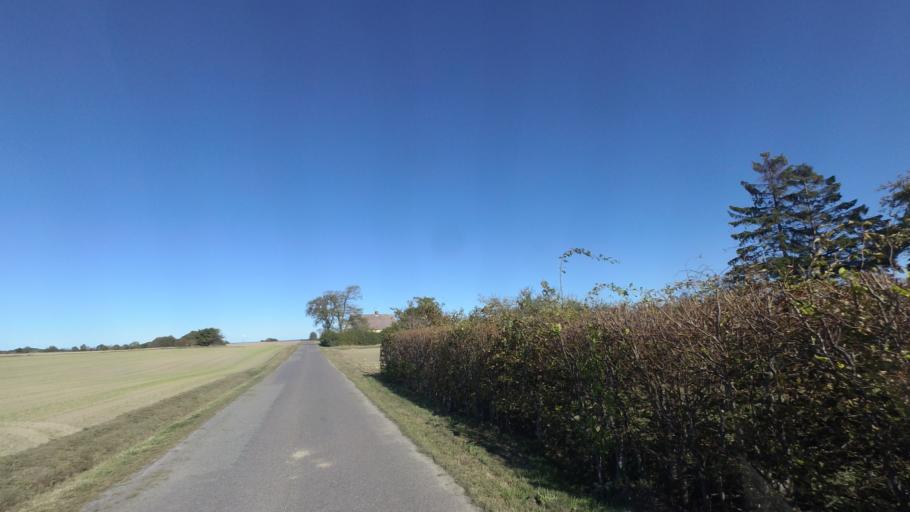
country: DK
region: Capital Region
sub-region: Bornholm Kommune
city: Nexo
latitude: 55.1163
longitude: 15.0439
